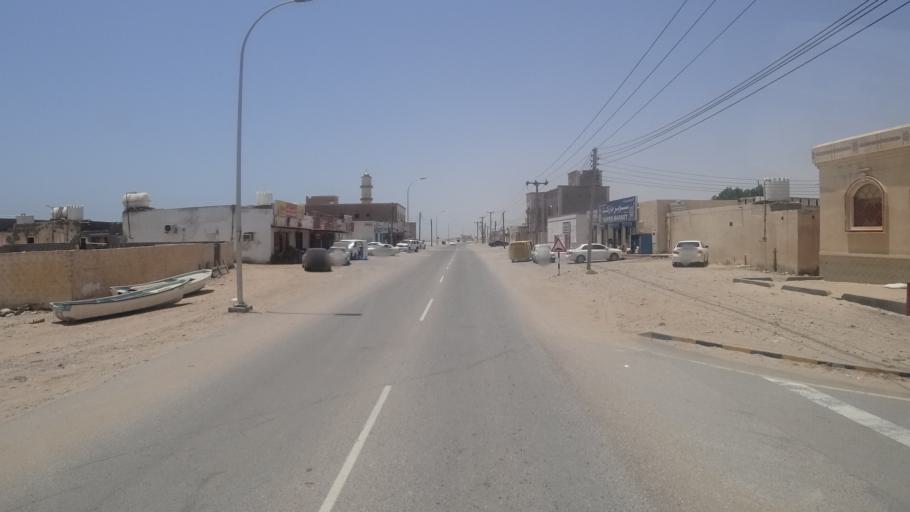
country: OM
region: Ash Sharqiyah
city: Sur
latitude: 22.0833
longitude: 59.6853
